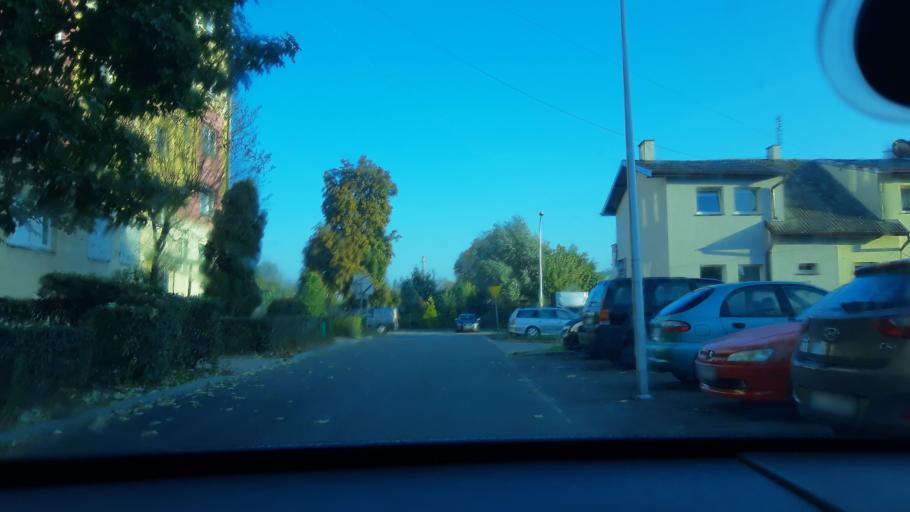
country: PL
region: Lodz Voivodeship
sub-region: Powiat sieradzki
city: Sieradz
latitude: 51.5934
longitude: 18.7221
